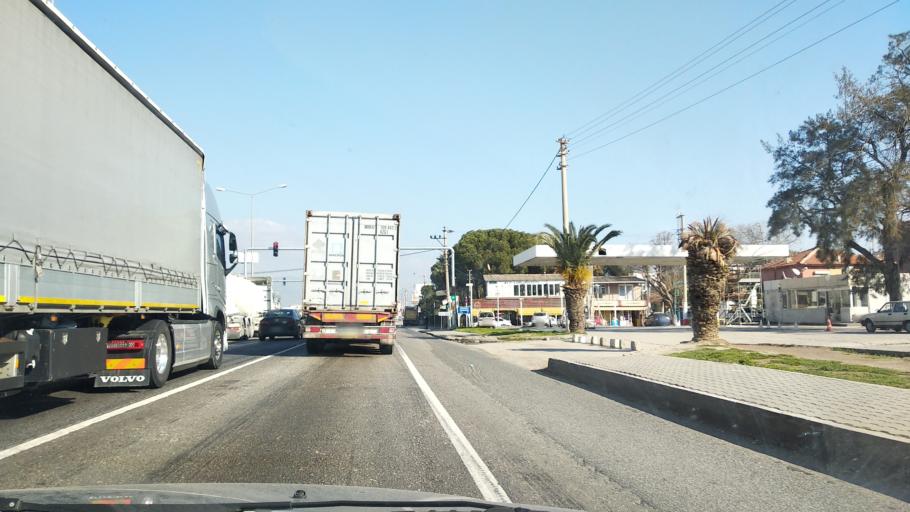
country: TR
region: Izmir
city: Menemen
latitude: 38.5763
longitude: 27.0629
